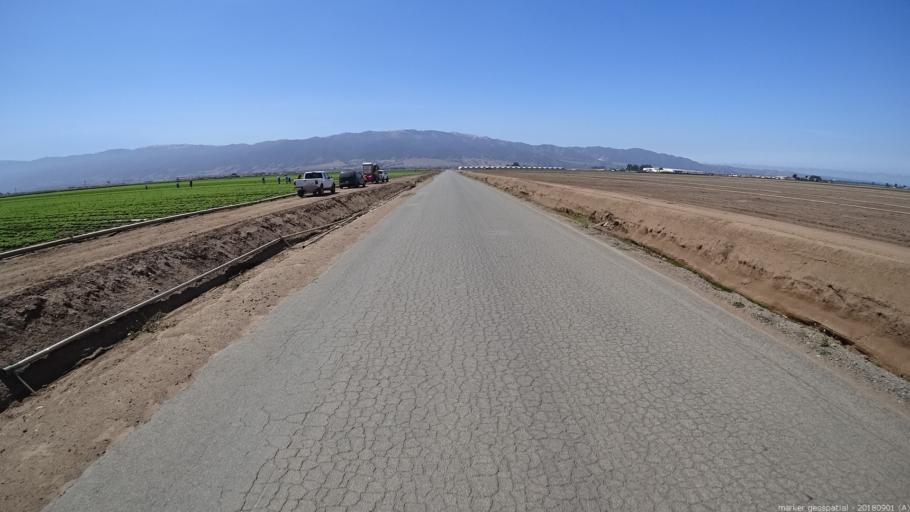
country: US
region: California
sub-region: Monterey County
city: Chualar
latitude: 36.5959
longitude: -121.5269
